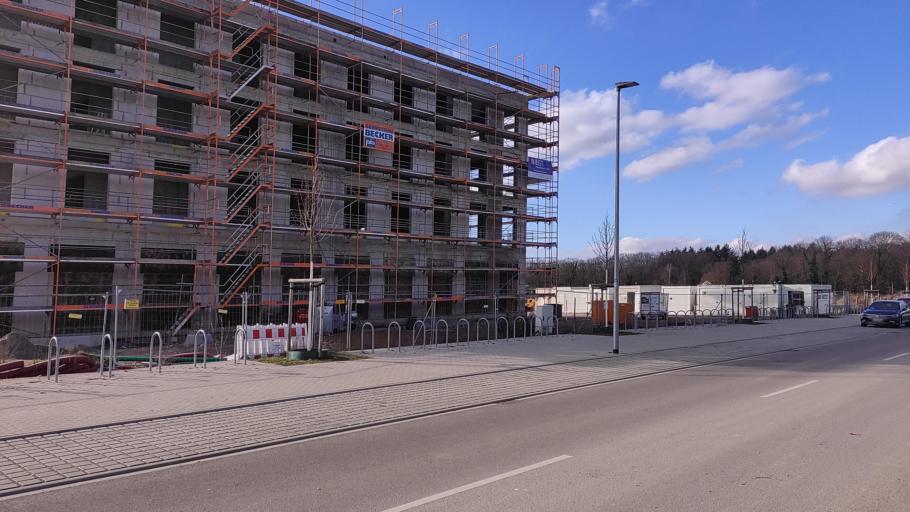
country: DE
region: Baden-Wuerttemberg
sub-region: Freiburg Region
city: Freiburg
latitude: 48.0201
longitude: 7.8291
